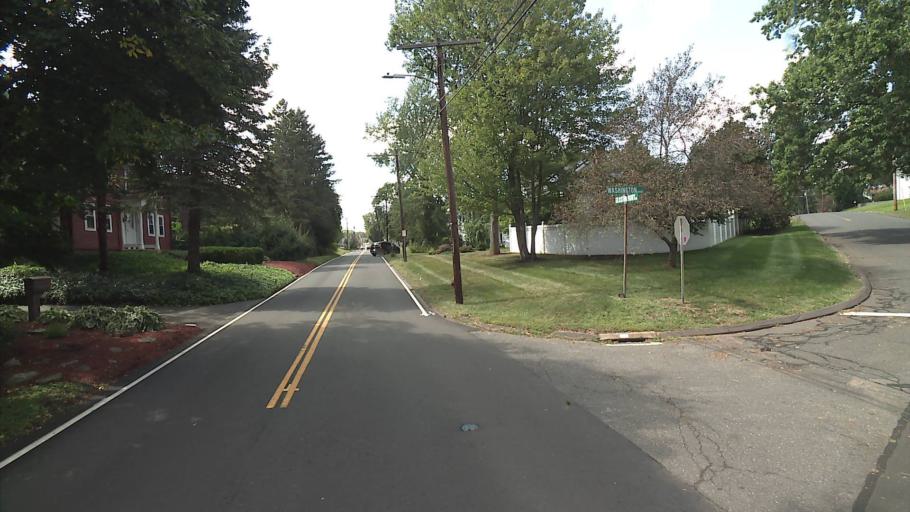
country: US
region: Connecticut
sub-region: Hartford County
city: Glastonbury Center
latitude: 41.6649
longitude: -72.6331
